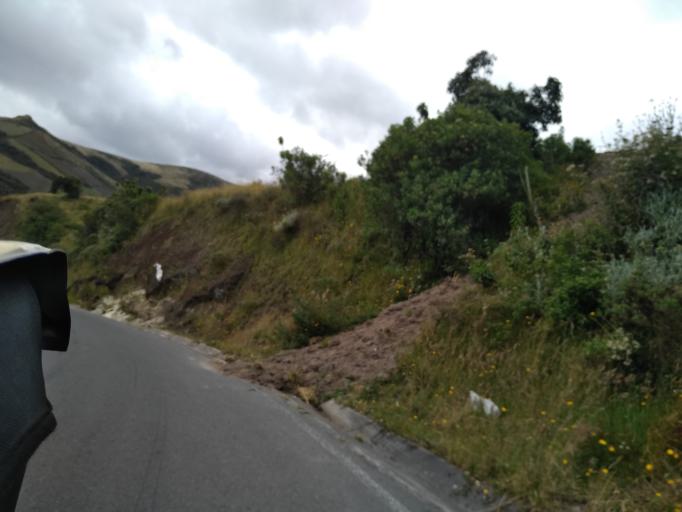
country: EC
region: Cotopaxi
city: Saquisili
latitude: -0.7252
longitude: -78.7531
